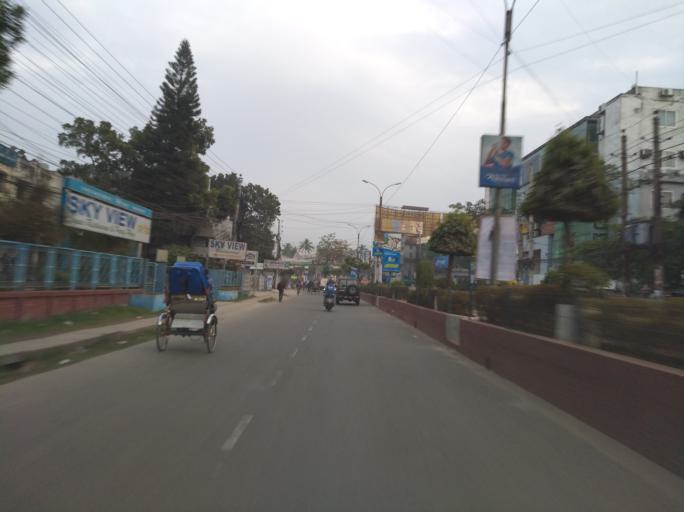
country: BD
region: Khulna
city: Khulna
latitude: 22.8236
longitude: 89.5524
